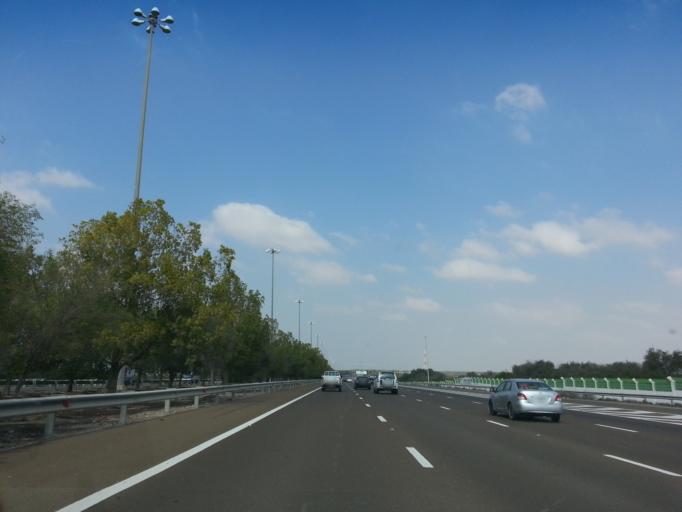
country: AE
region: Dubai
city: Dubai
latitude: 24.8005
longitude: 54.8645
